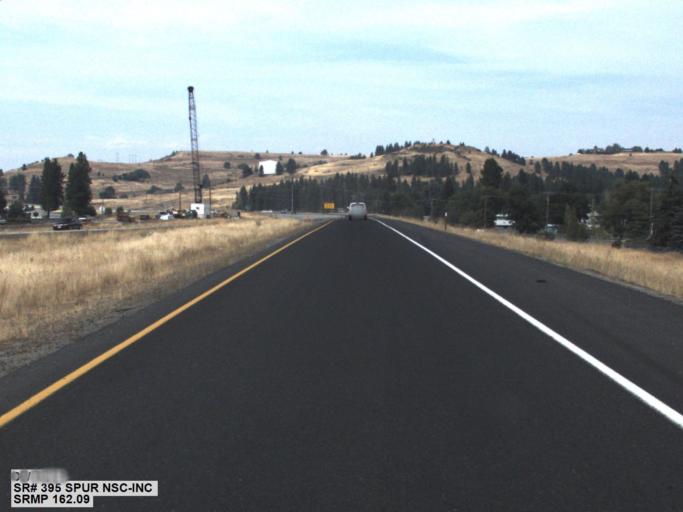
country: US
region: Washington
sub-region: Spokane County
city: Mead
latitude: 47.7737
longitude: -117.3729
